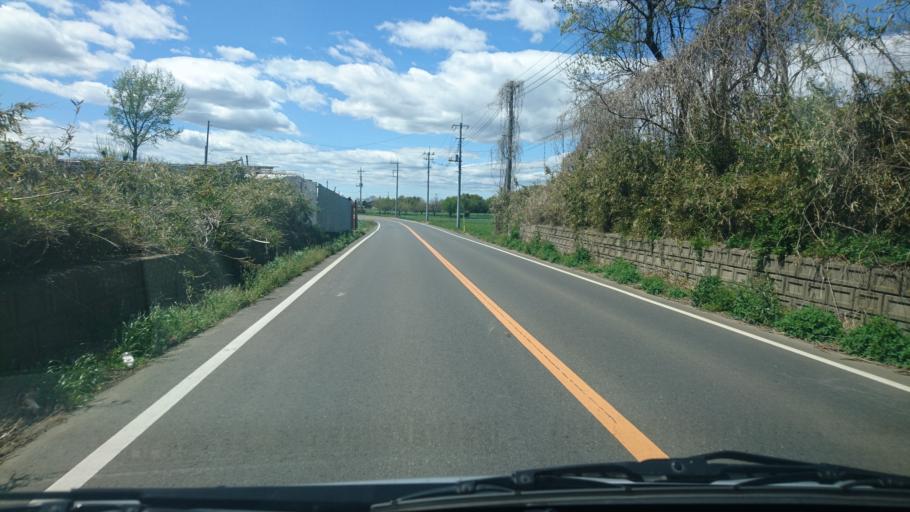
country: JP
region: Ibaraki
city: Yuki
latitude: 36.2759
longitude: 139.9173
